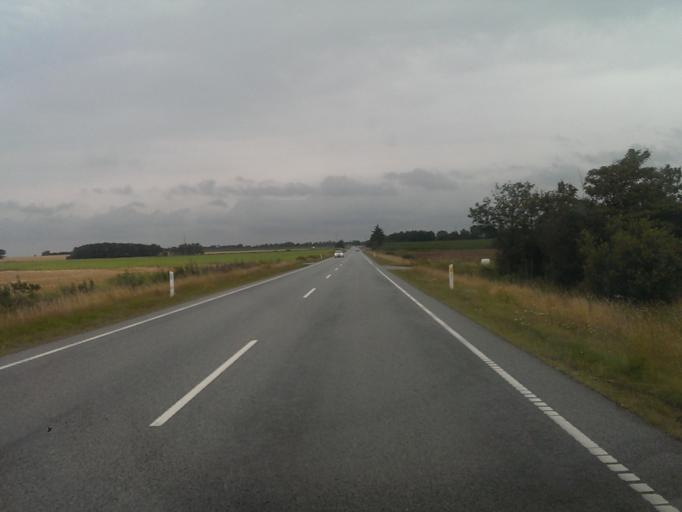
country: DK
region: South Denmark
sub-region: Esbjerg Kommune
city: Bramming
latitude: 55.5558
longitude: 8.6416
